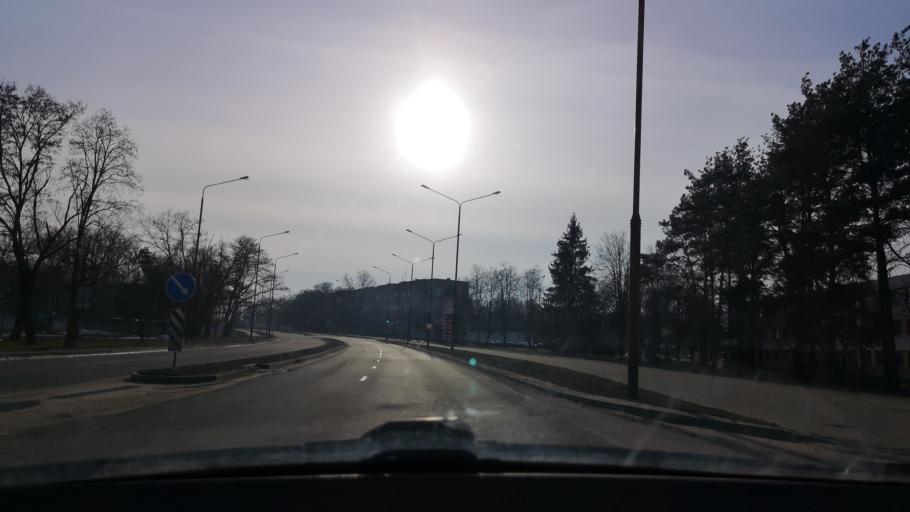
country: BY
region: Brest
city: Brest
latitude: 52.1393
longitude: 23.6772
